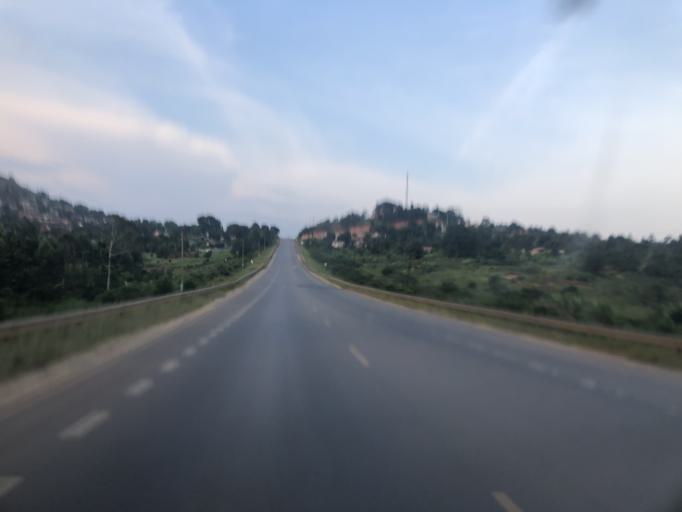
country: UG
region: Central Region
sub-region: Mpigi District
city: Mpigi
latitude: 0.2138
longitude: 32.3249
